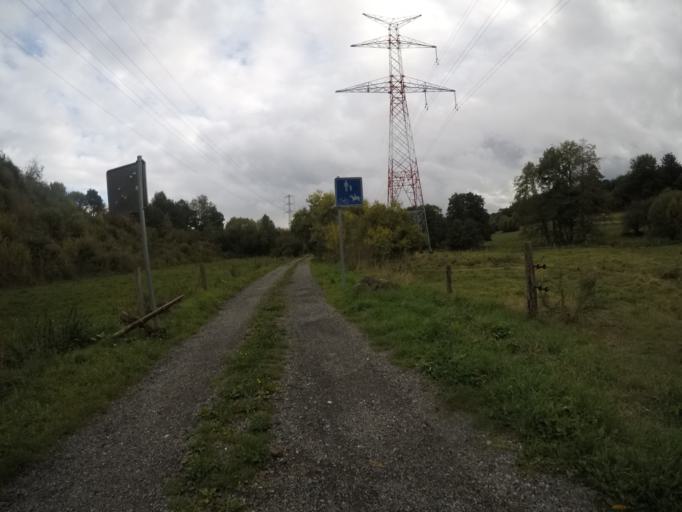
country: BE
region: Wallonia
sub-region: Province du Luxembourg
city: Fauvillers
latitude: 49.9025
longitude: 5.6864
